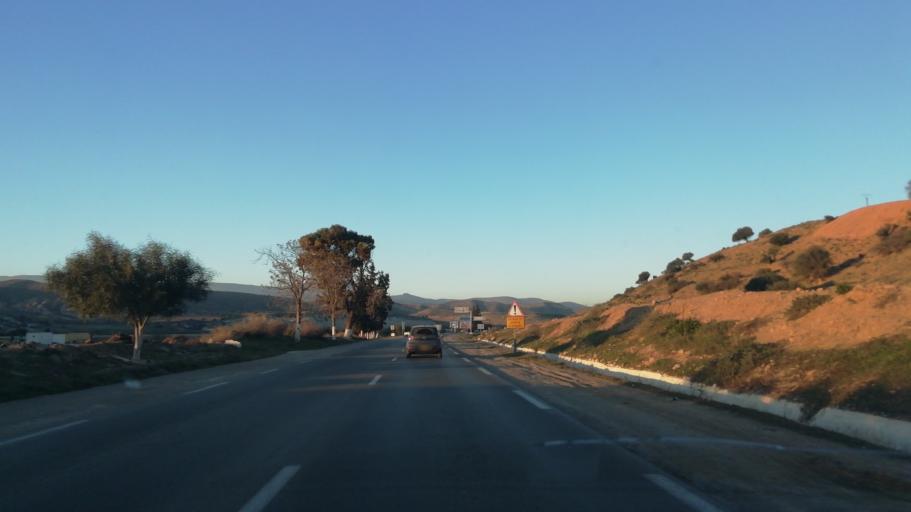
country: DZ
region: Tlemcen
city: Nedroma
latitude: 34.9036
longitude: -1.6403
